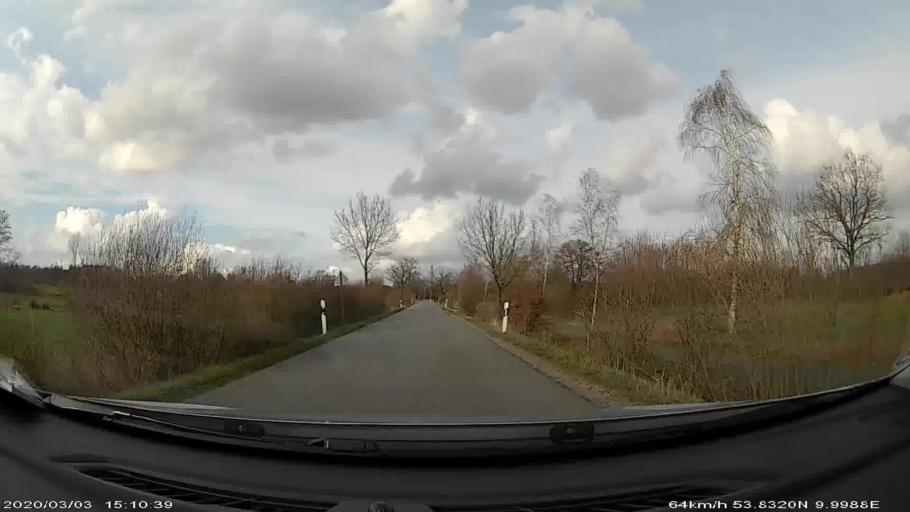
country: DE
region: Schleswig-Holstein
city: Oersdorf
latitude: 53.8316
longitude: 9.9989
